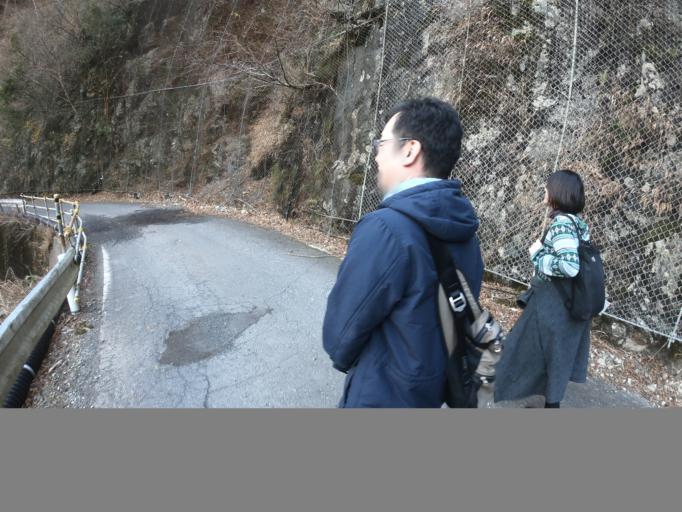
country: JP
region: Shizuoka
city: Shizuoka-shi
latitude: 35.1781
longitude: 138.1095
